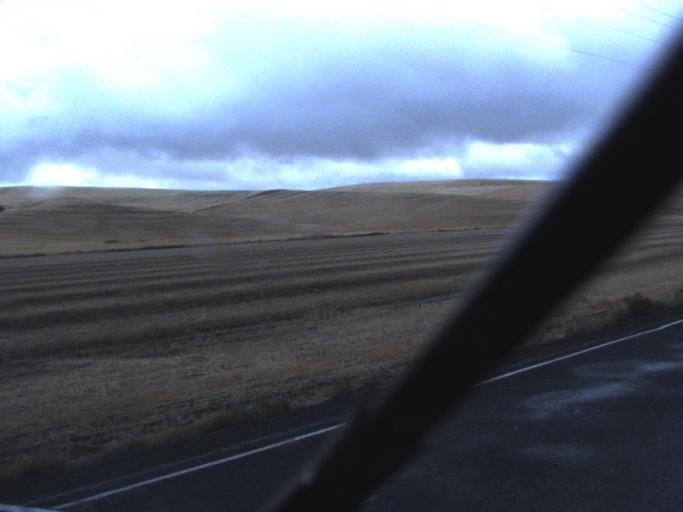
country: US
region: Washington
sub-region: Whitman County
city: Colfax
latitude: 47.0292
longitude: -117.4969
